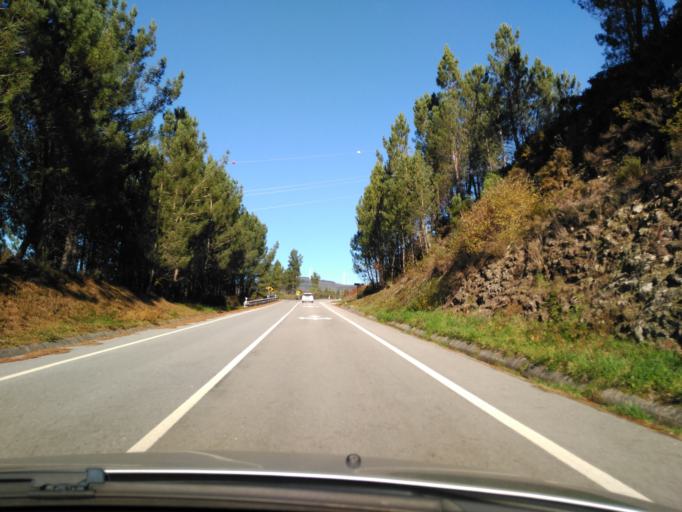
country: PT
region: Braga
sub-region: Cabeceiras de Basto
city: Cabeceiras de Basto
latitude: 41.6875
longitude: -7.9533
